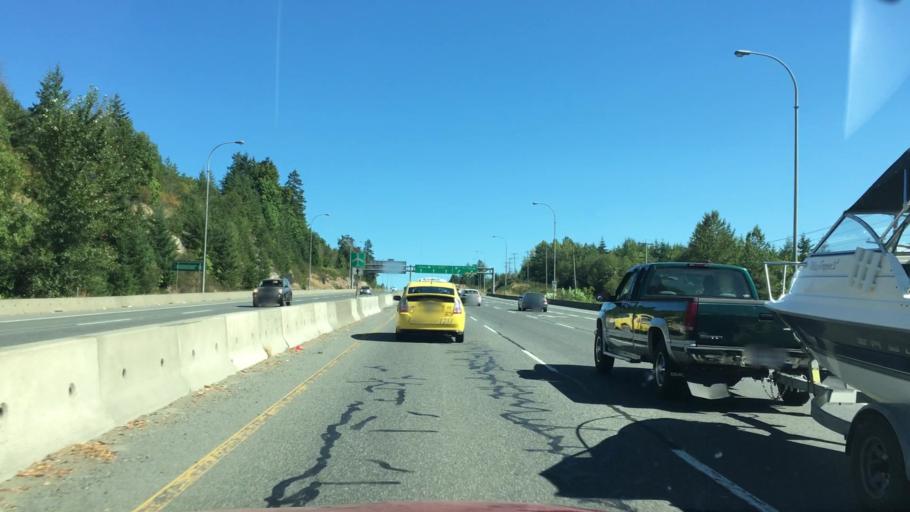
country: CA
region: British Columbia
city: Nanaimo
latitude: 49.1174
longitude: -123.9109
